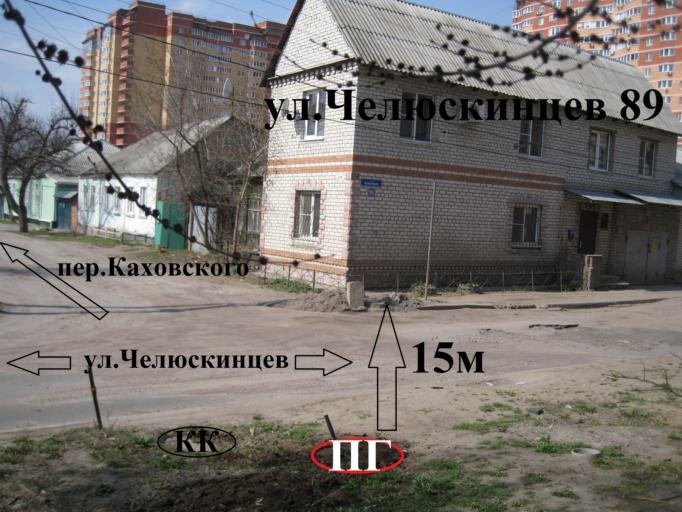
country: RU
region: Voronezj
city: Voronezh
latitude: 51.6477
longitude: 39.1933
